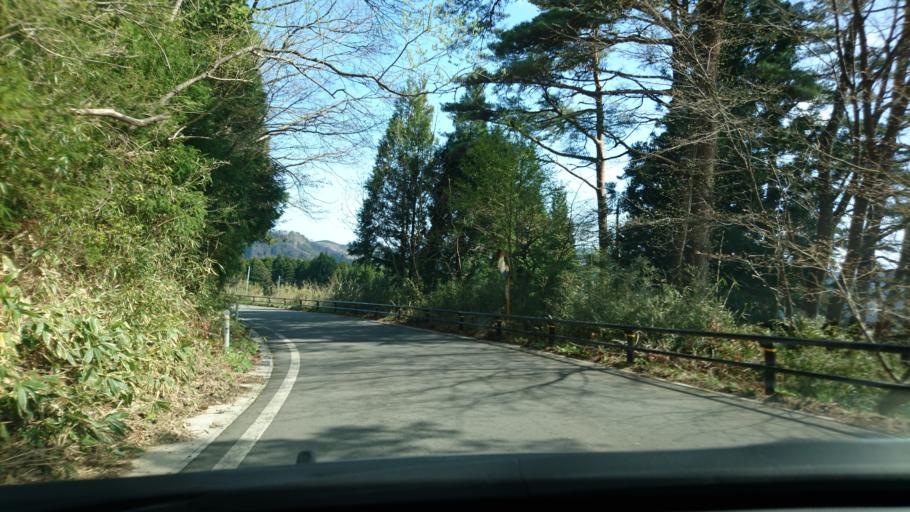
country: JP
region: Iwate
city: Ofunato
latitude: 38.9576
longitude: 141.4502
